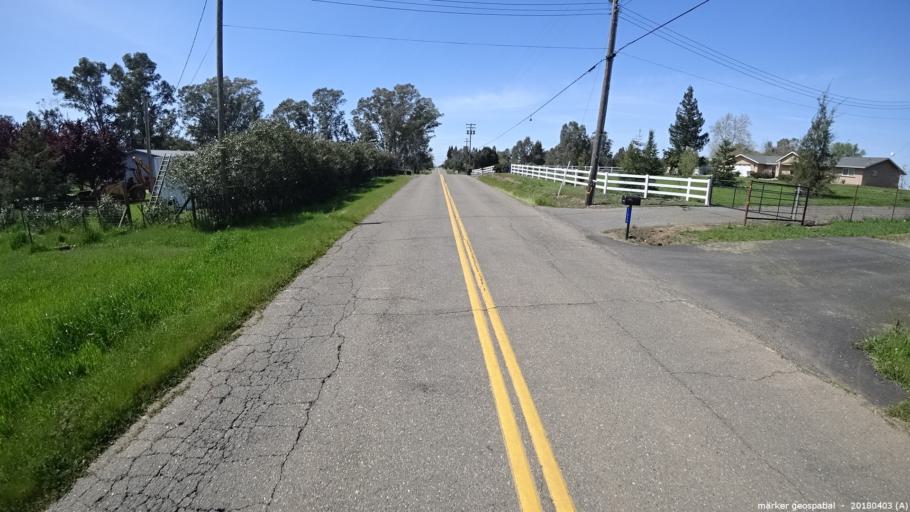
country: US
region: California
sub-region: Sacramento County
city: Wilton
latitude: 38.3796
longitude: -121.2317
